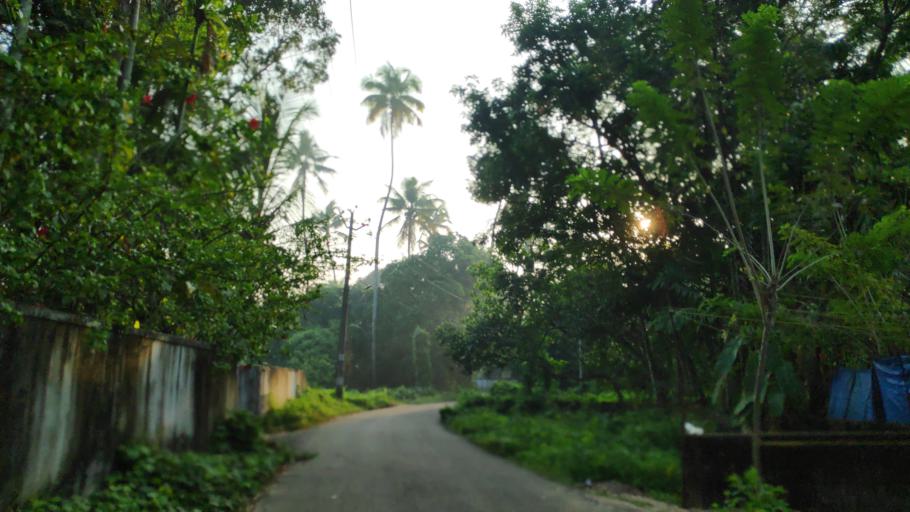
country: IN
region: Kerala
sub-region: Alappuzha
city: Vayalar
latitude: 9.6639
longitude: 76.2969
